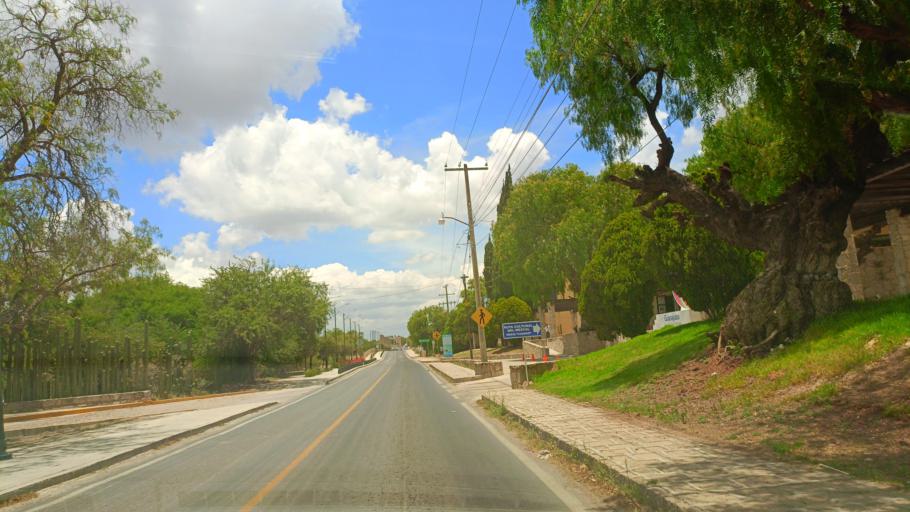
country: MX
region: Guanajuato
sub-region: San Luis de la Paz
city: San Ignacio
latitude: 21.2304
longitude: -100.4908
